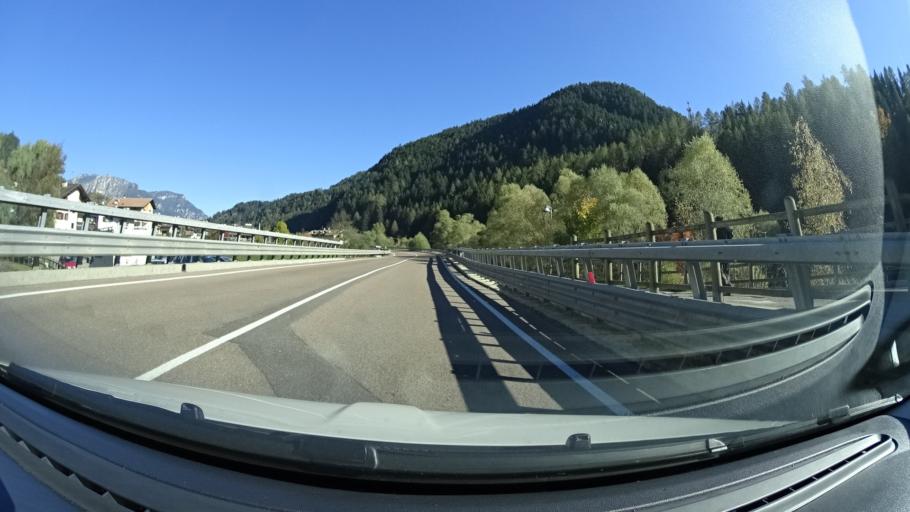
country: IT
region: Trentino-Alto Adige
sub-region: Provincia di Trento
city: Castello Molina di Fiemme
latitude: 46.2710
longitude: 11.4146
